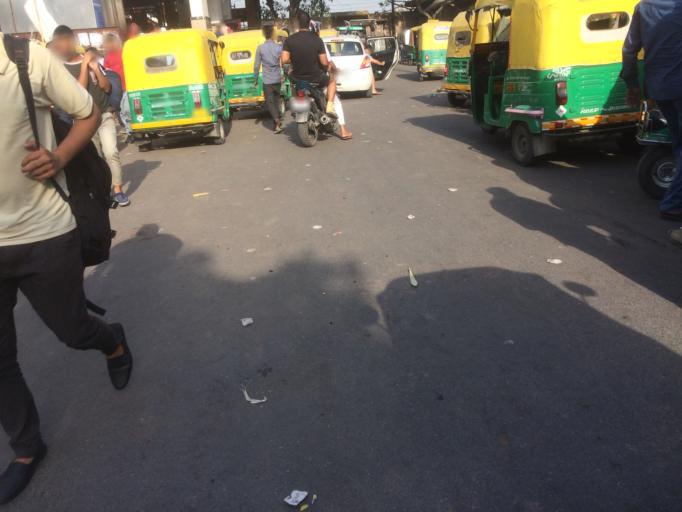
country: IN
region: NCT
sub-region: New Delhi
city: New Delhi
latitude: 28.5888
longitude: 77.2554
